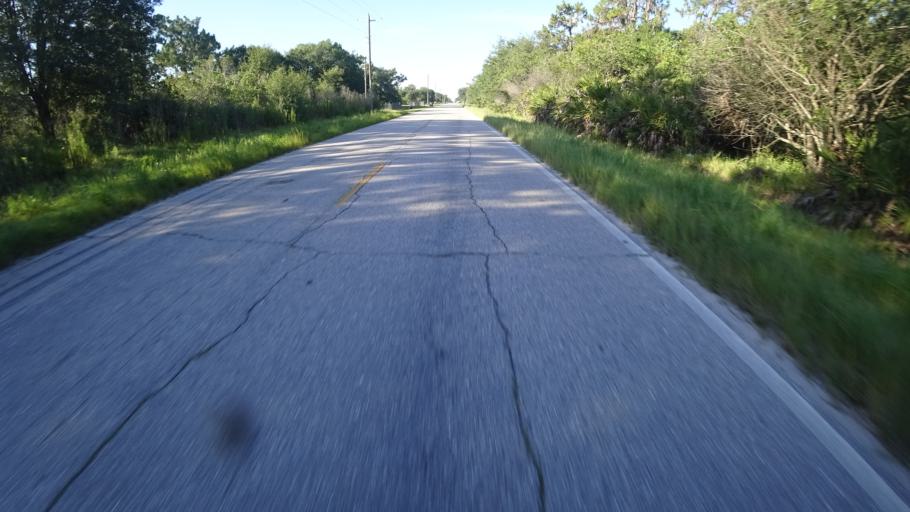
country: US
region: Florida
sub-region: Sarasota County
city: The Meadows
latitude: 27.4265
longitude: -82.2708
